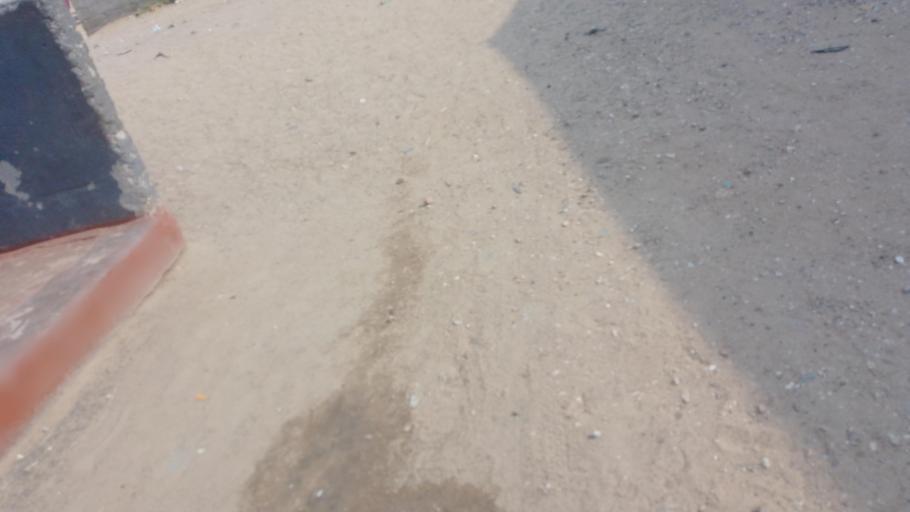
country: ZM
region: Lusaka
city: Lusaka
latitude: -15.4059
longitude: 28.3732
